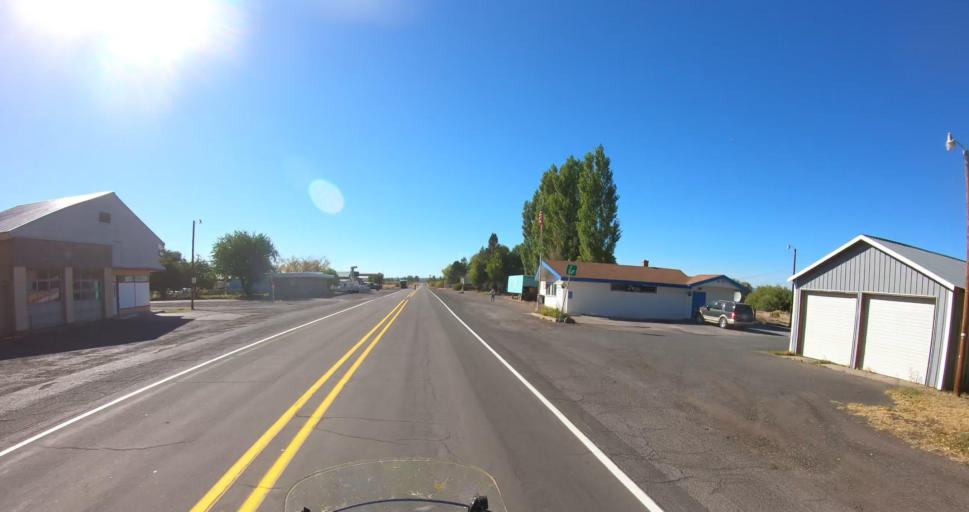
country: US
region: Oregon
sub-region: Deschutes County
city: La Pine
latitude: 43.1276
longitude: -121.0480
